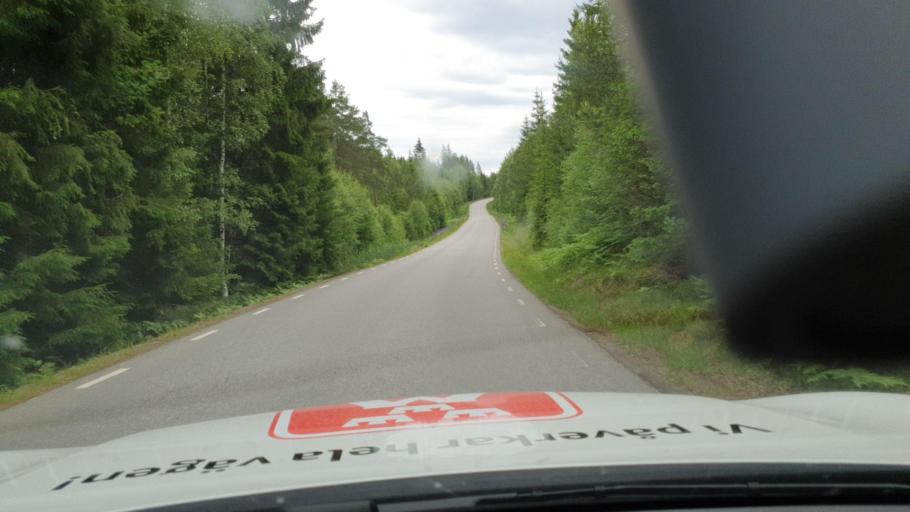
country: SE
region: Vaestra Goetaland
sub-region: Karlsborgs Kommun
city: Karlsborg
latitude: 58.6665
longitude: 14.4291
